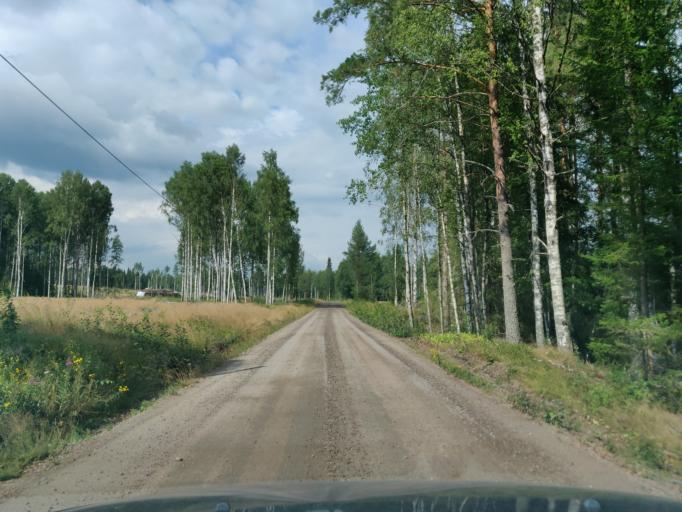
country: SE
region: Vaermland
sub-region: Hagfors Kommun
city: Hagfors
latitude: 59.9901
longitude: 13.5651
